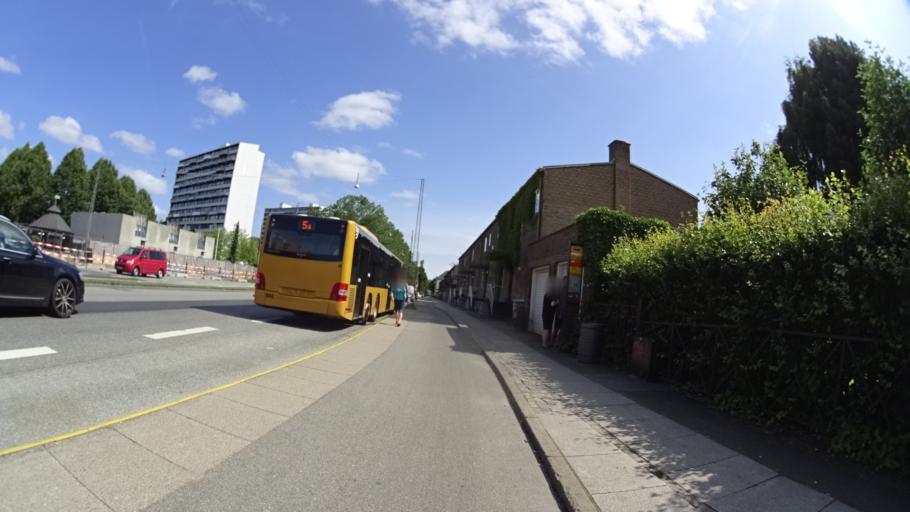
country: DK
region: Central Jutland
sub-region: Arhus Kommune
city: Arhus
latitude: 56.1402
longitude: 10.1951
